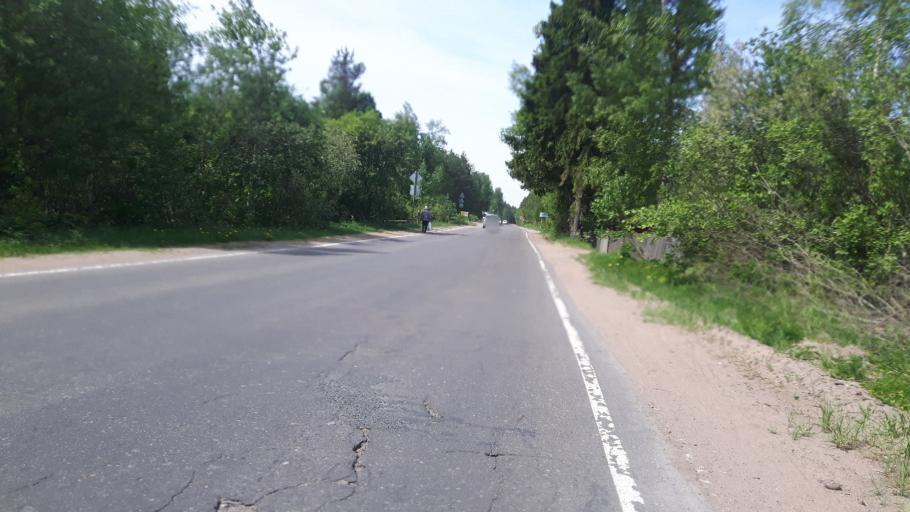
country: RU
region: Leningrad
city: Ust'-Luga
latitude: 59.6572
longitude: 28.2523
